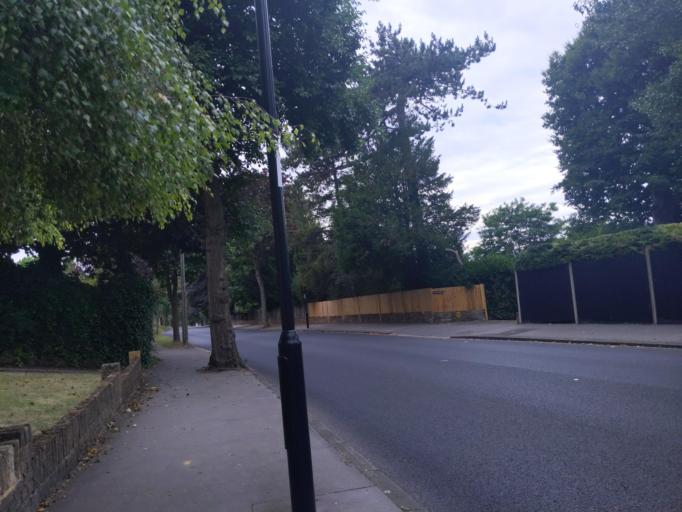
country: GB
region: England
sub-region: Greater London
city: South Croydon
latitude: 51.3546
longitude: -0.0855
